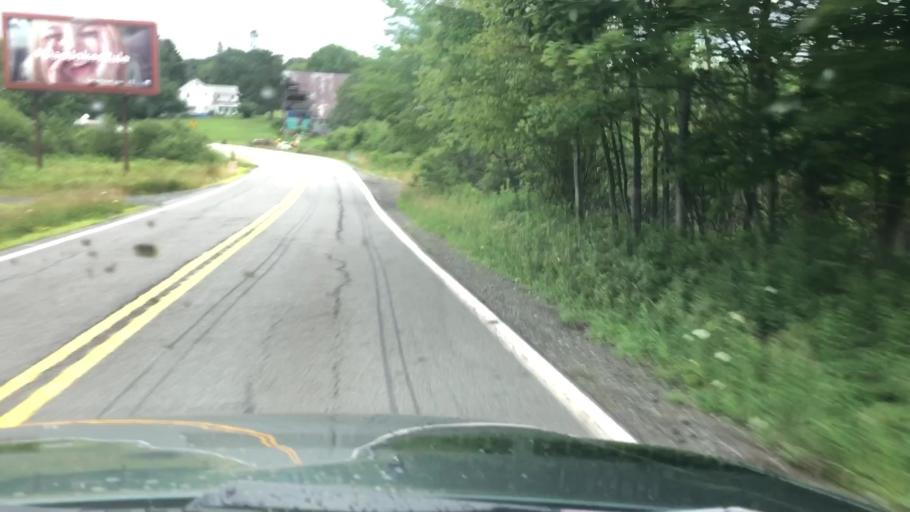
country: US
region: Pennsylvania
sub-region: Monroe County
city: Mountainhome
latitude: 41.2918
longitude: -75.2215
